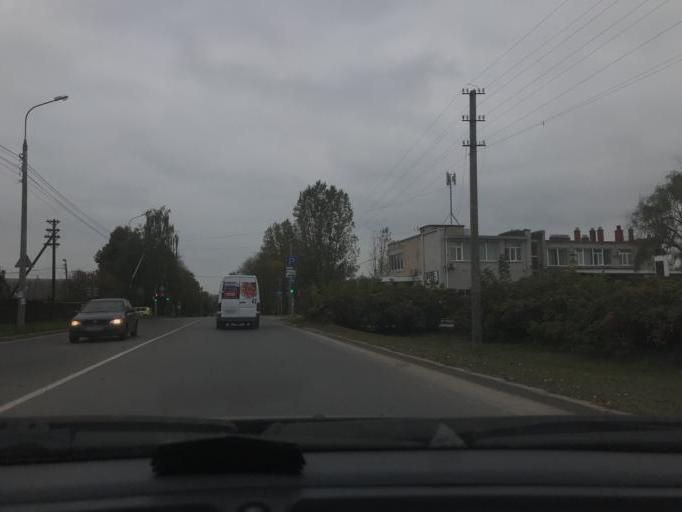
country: RU
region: Kaluga
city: Kaluga
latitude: 54.5156
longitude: 36.3177
